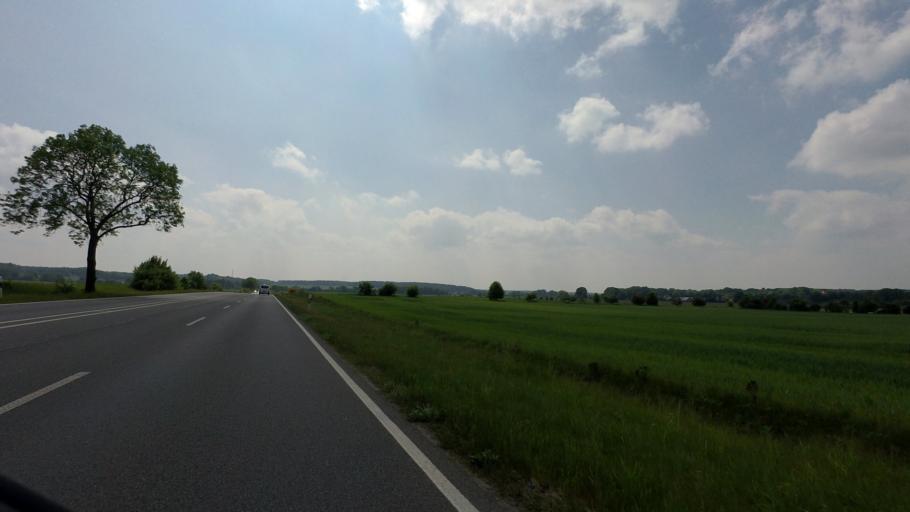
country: DE
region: Brandenburg
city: Cottbus
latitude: 51.6719
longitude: 14.3566
